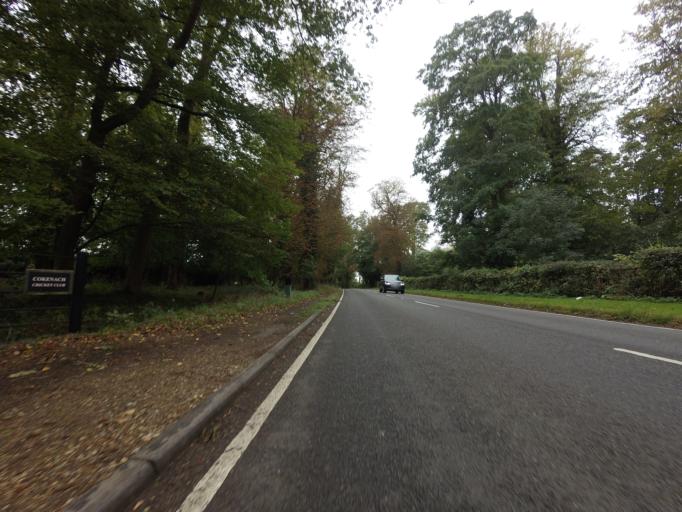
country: GB
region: England
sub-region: Hertfordshire
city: Reed
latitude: 52.0082
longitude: 0.0221
